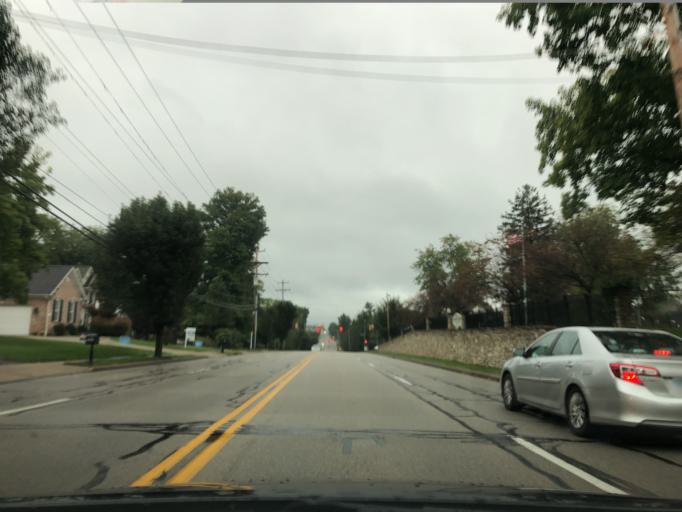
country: US
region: Ohio
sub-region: Hamilton County
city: Rossmoyne
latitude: 39.2125
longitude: -84.3790
